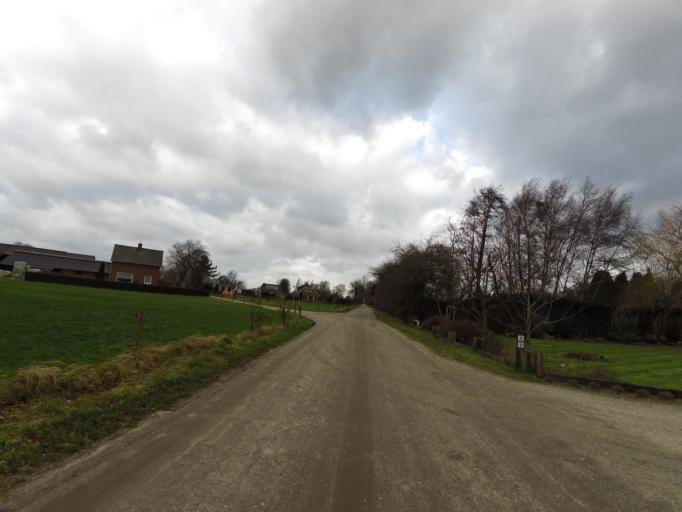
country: NL
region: Gelderland
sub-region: Gemeente Doetinchem
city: Doetinchem
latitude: 51.9330
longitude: 6.2519
